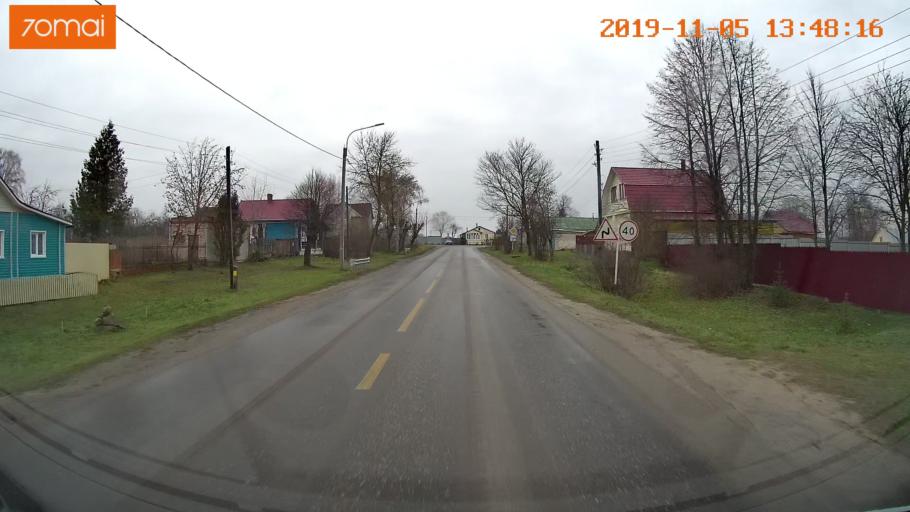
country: RU
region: Ivanovo
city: Shuya
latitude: 57.0032
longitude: 41.4054
